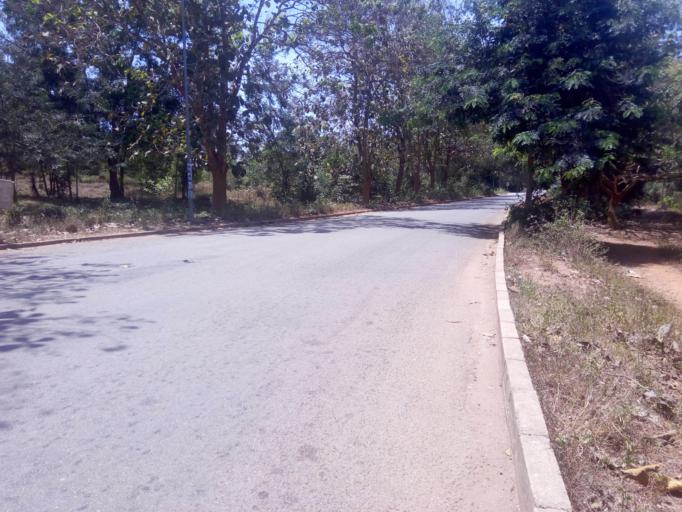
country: GH
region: Central
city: Cape Coast
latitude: 5.1302
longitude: -1.2903
